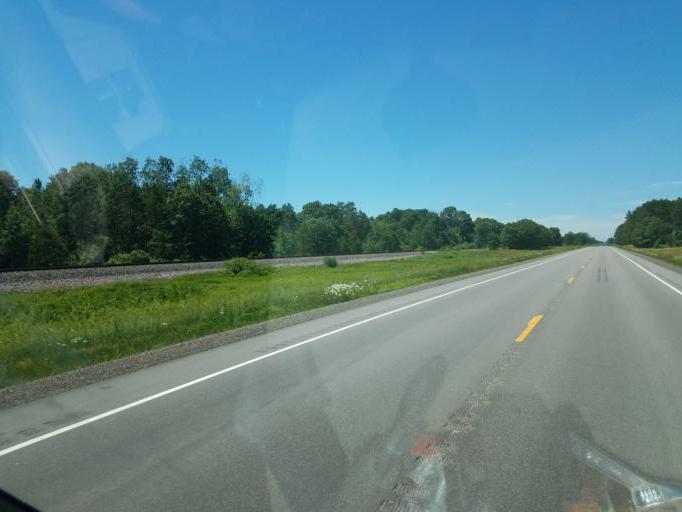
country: US
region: Wisconsin
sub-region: Juneau County
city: New Lisbon
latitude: 44.0249
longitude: -90.1400
